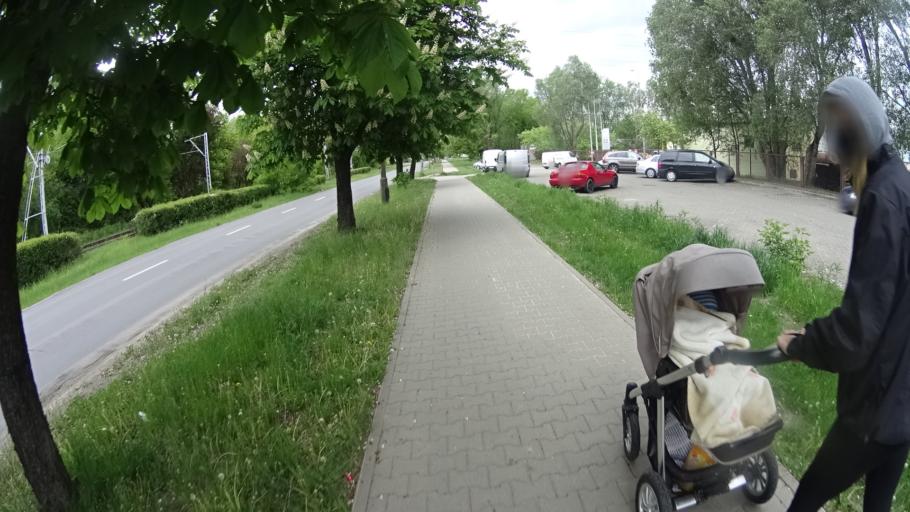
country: PL
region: Masovian Voivodeship
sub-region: Warszawa
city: Bielany
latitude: 52.2829
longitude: 20.9210
